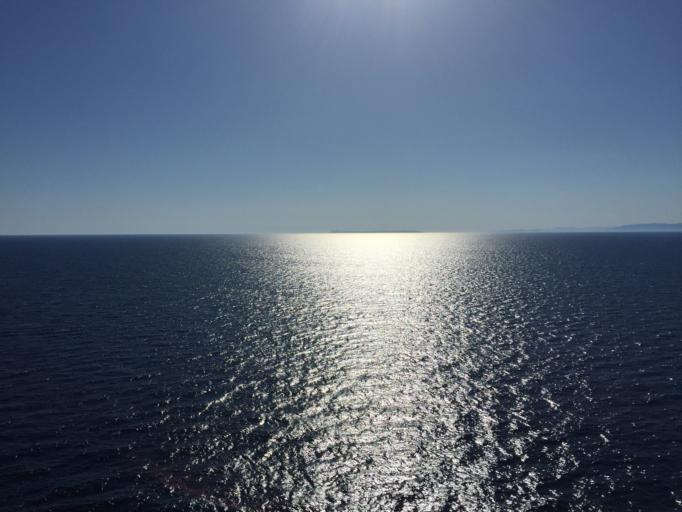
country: FR
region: Provence-Alpes-Cote d'Azur
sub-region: Departement du Var
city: Ramatuelle
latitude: 43.0676
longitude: 6.8459
